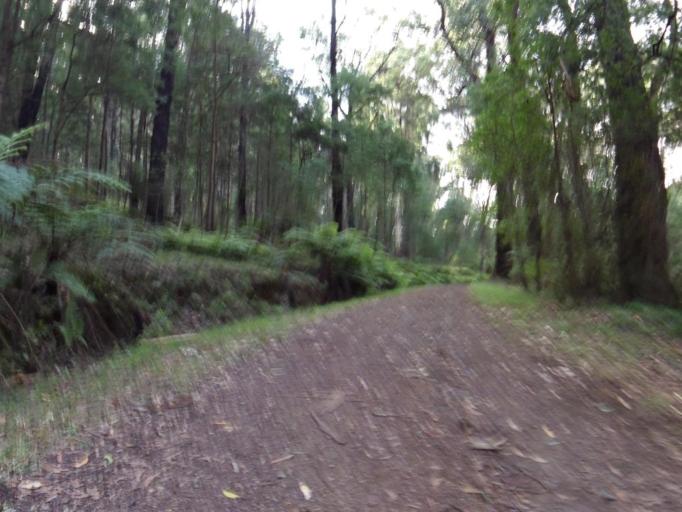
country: AU
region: Victoria
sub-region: Yarra Ranges
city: Kalorama
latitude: -37.8242
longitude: 145.4012
